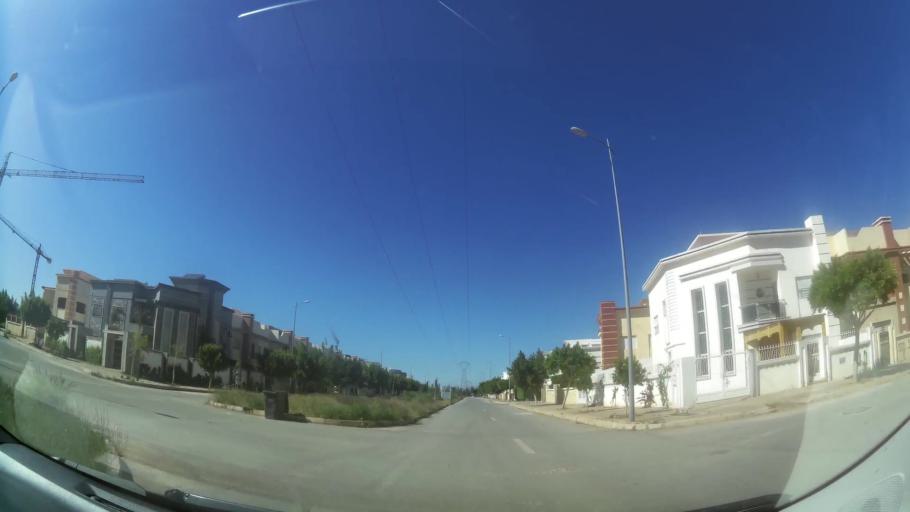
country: MA
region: Oriental
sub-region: Oujda-Angad
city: Oujda
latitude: 34.7235
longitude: -1.9099
